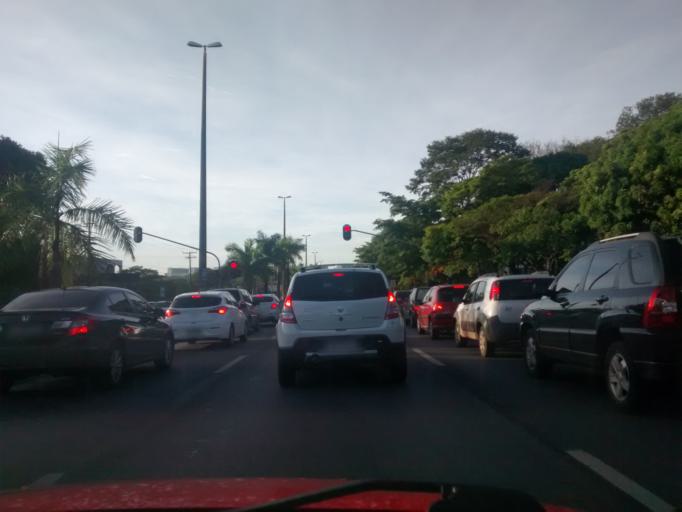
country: BR
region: Federal District
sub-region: Brasilia
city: Brasilia
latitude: -15.7759
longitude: -47.8744
